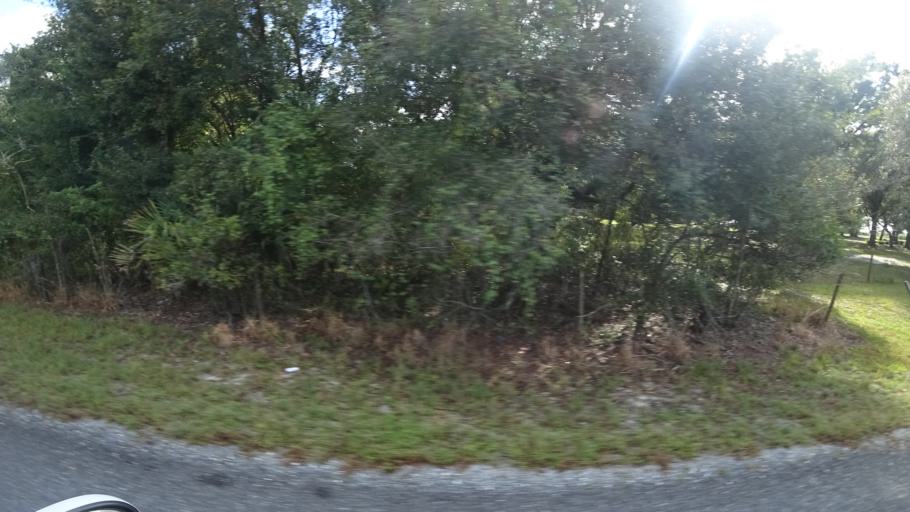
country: US
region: Florida
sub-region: Hillsborough County
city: Wimauma
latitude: 27.4614
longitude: -82.1531
